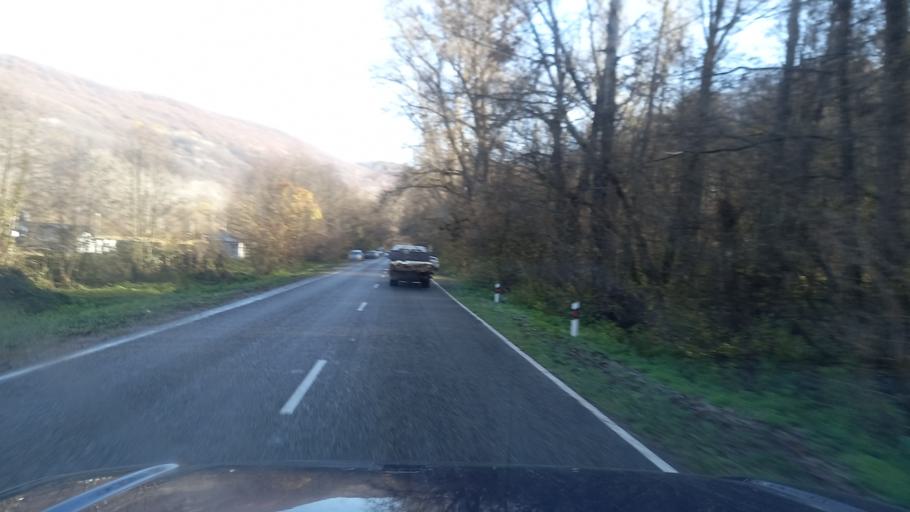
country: RU
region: Krasnodarskiy
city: Goryachiy Klyuch
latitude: 44.5971
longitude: 39.0854
